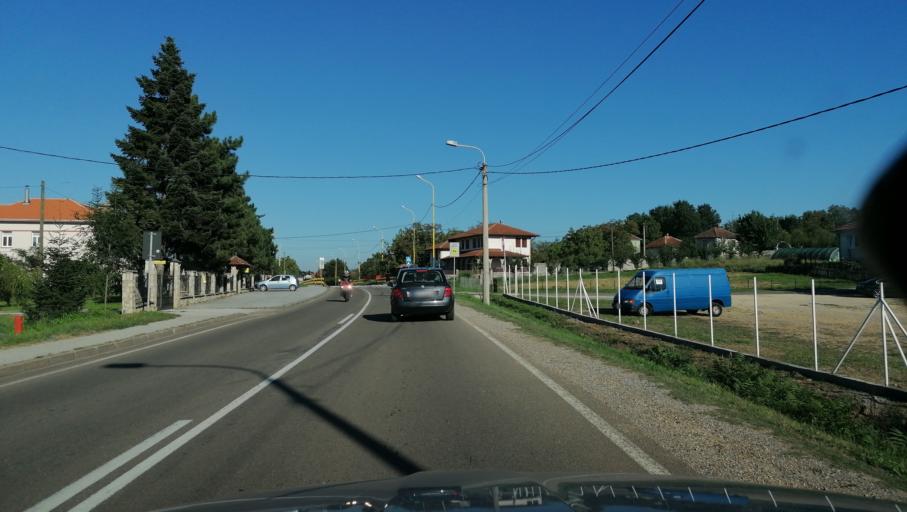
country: RS
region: Central Serbia
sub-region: Sumadijski Okrug
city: Knic
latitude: 43.9274
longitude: 20.7114
